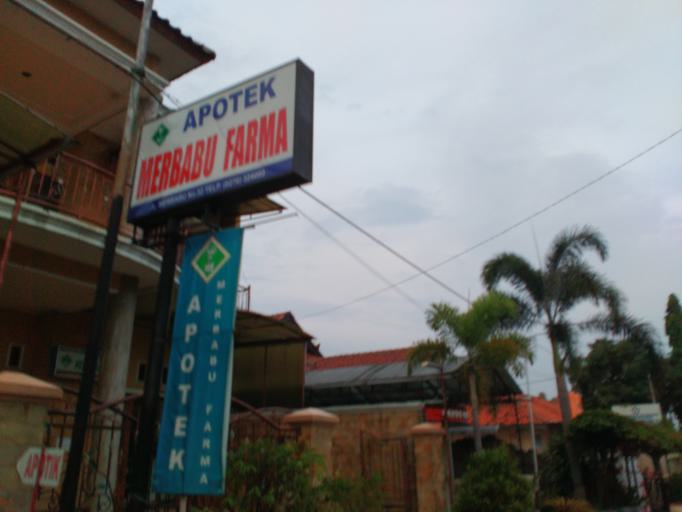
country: ID
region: Central Java
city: Boyolali
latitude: -7.5316
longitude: 110.5983
